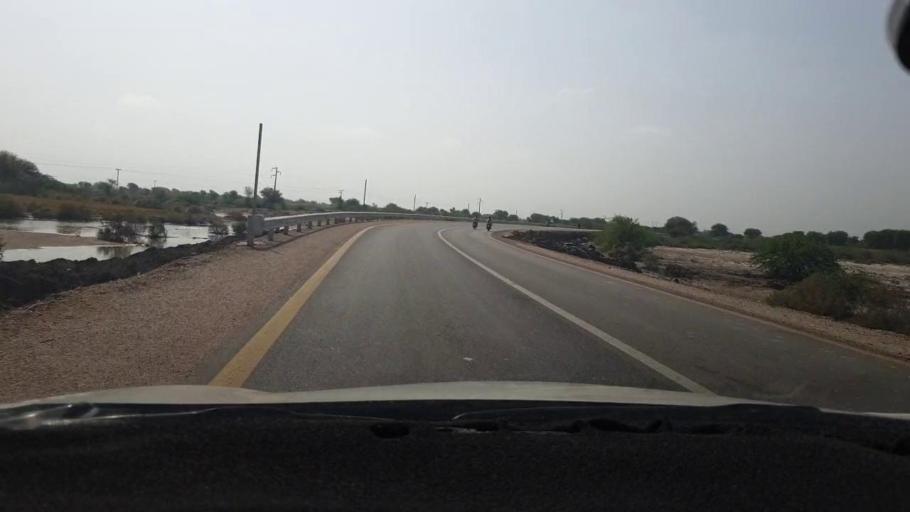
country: PK
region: Sindh
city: Jhol
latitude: 25.8583
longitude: 69.0589
